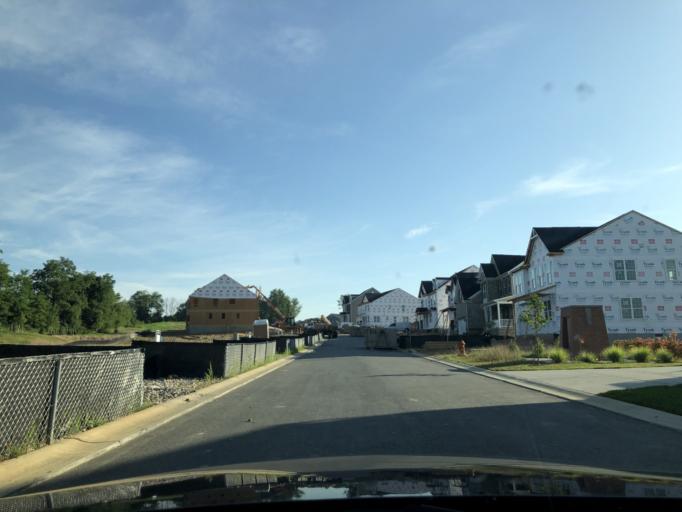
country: US
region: Maryland
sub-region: Howard County
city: Highland
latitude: 39.1981
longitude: -76.9436
